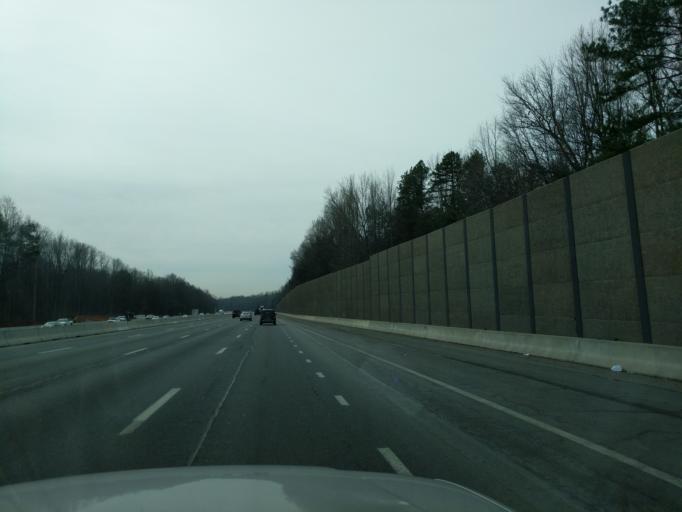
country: US
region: North Carolina
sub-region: Mecklenburg County
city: Charlotte
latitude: 35.3006
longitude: -80.8500
